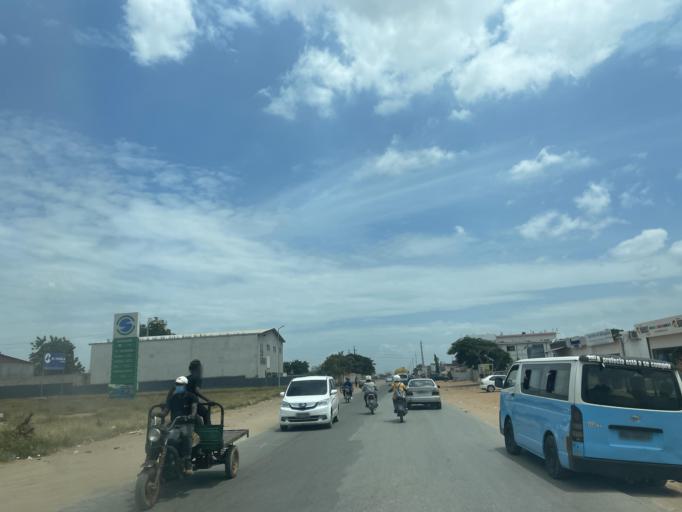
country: AO
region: Luanda
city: Luanda
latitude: -8.9346
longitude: 13.3819
